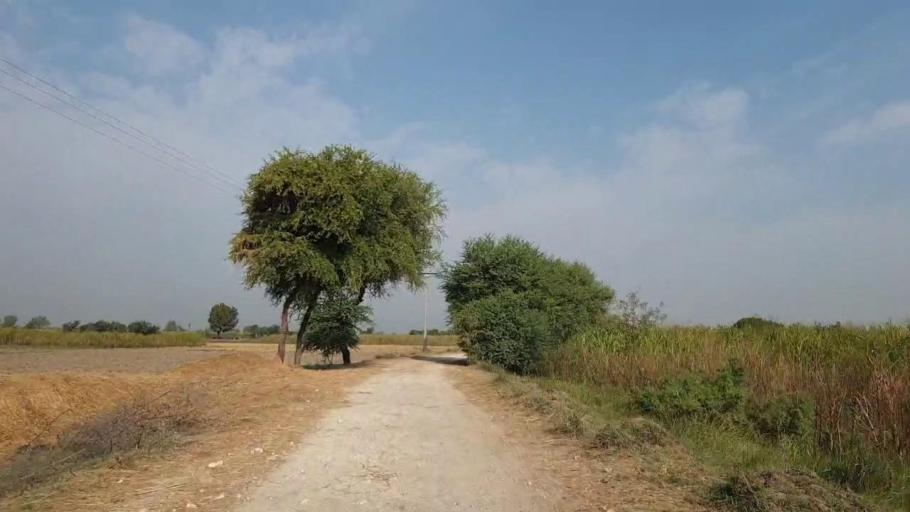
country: PK
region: Sindh
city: Tando Muhammad Khan
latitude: 25.0473
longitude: 68.4362
